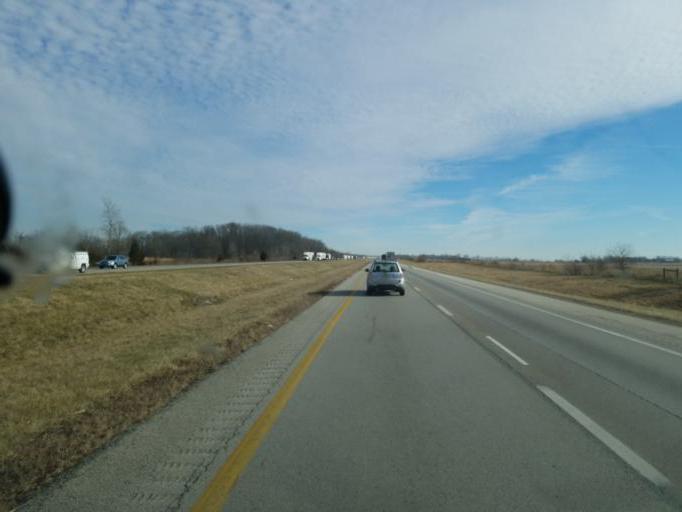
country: US
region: Ohio
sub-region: Preble County
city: Lewisburg
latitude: 39.8377
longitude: -84.4987
